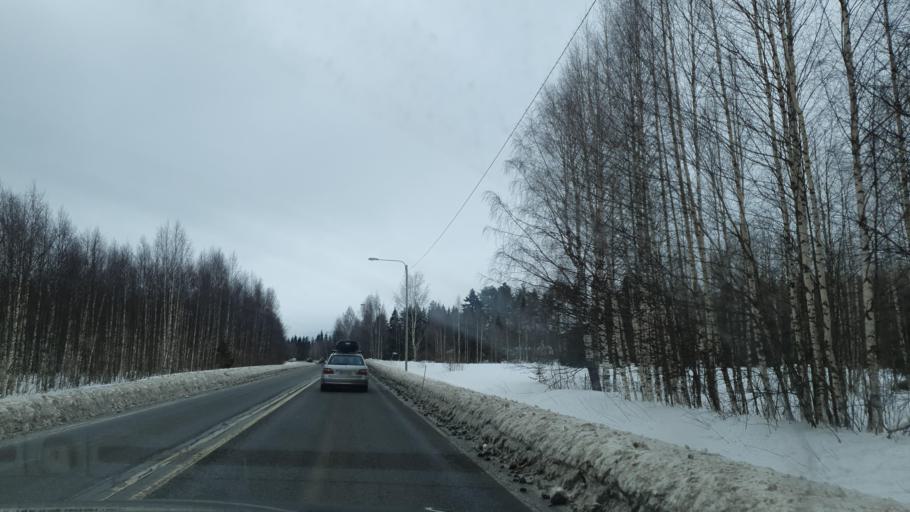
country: FI
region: Lapland
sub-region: Kemi-Tornio
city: Tornio
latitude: 66.0954
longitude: 23.9468
